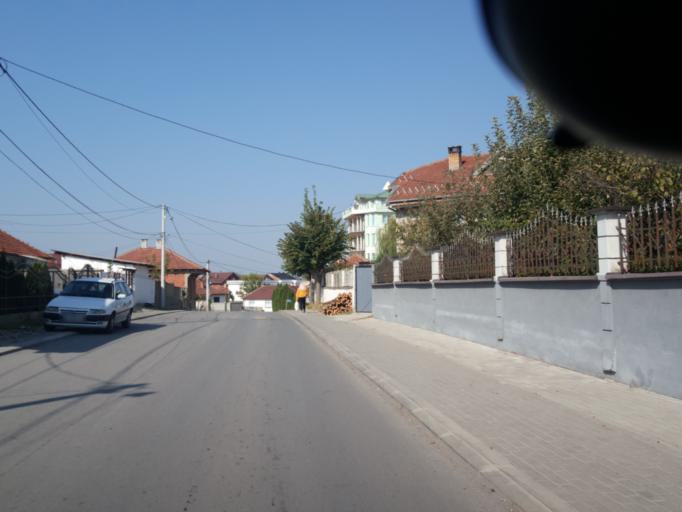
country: XK
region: Gjakova
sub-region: Komuna e Gjakoves
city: Gjakove
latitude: 42.3927
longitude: 20.4293
